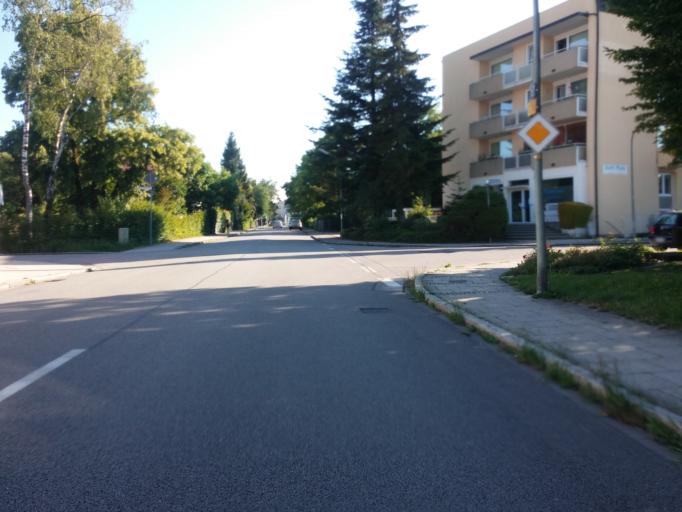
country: DE
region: Bavaria
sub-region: Upper Bavaria
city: Vaterstetten
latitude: 48.1038
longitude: 11.7905
